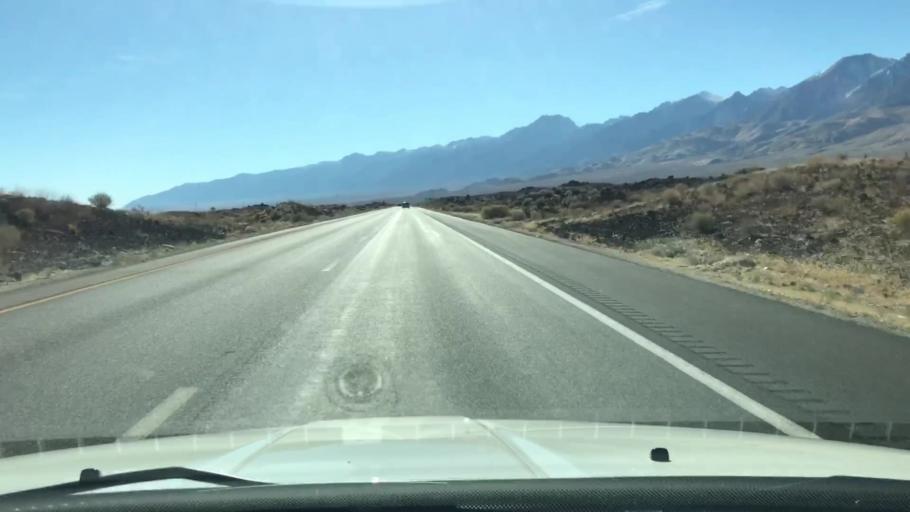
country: US
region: California
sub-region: Inyo County
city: Big Pine
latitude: 36.9395
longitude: -118.2409
